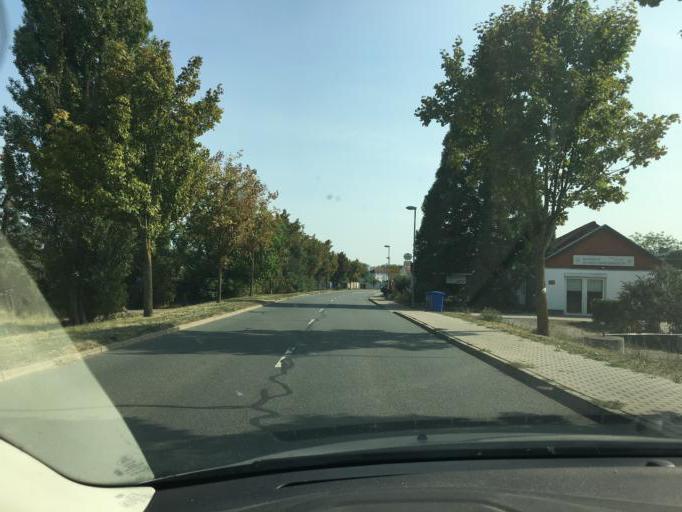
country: DE
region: Saxony-Anhalt
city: Barby
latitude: 51.9676
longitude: 11.8757
